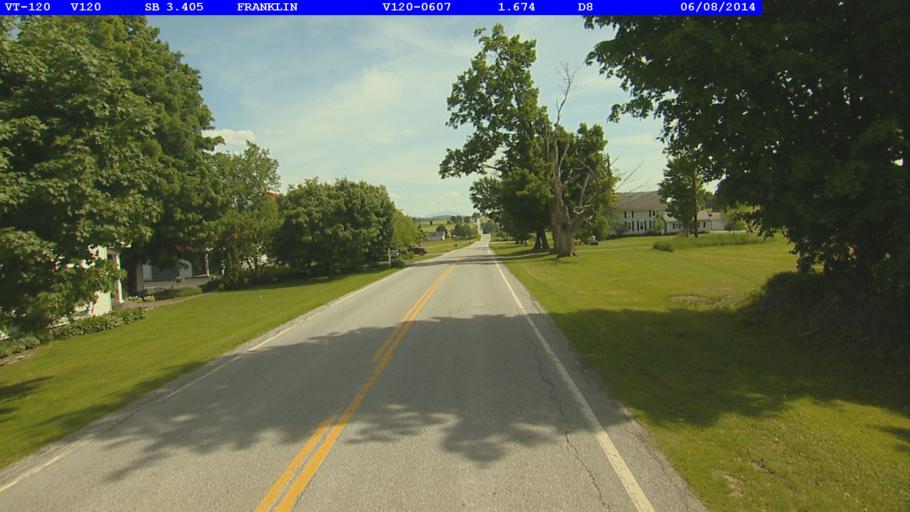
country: US
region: Vermont
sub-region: Franklin County
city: Enosburg Falls
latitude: 44.9571
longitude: -72.9061
